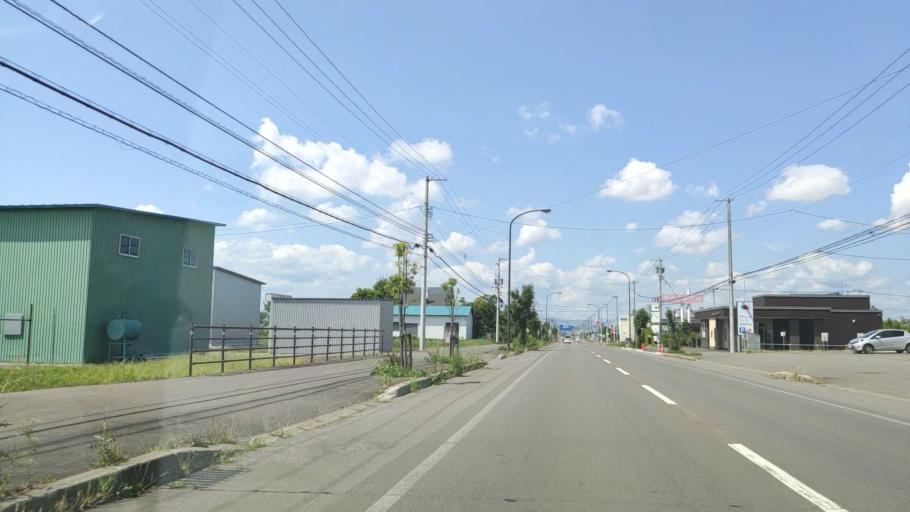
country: JP
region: Hokkaido
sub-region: Asahikawa-shi
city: Asahikawa
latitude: 43.7697
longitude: 142.4605
